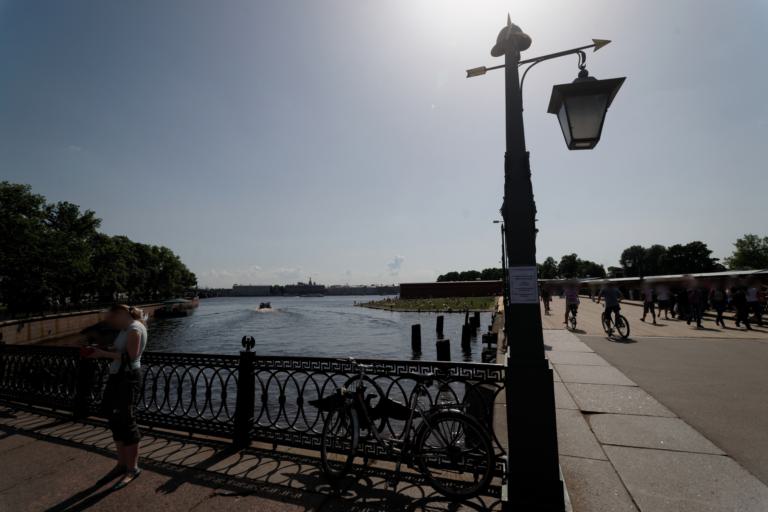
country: RU
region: St.-Petersburg
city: Saint Petersburg
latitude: 59.9527
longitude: 30.3228
